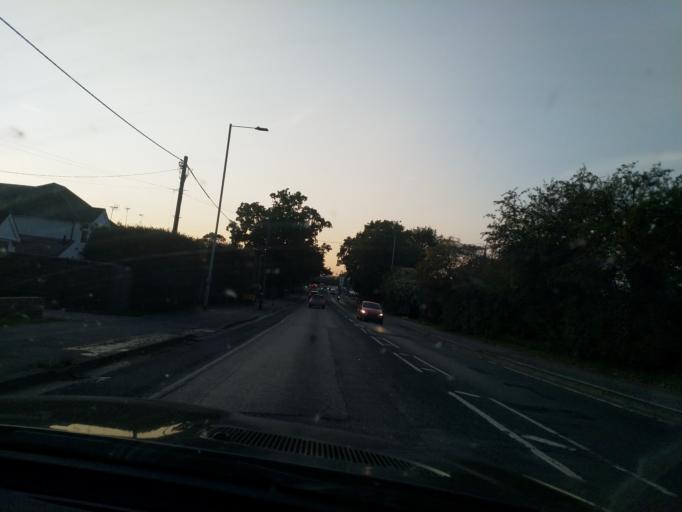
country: GB
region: England
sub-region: Kent
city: Leysdown-on-Sea
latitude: 51.4228
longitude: 0.8643
